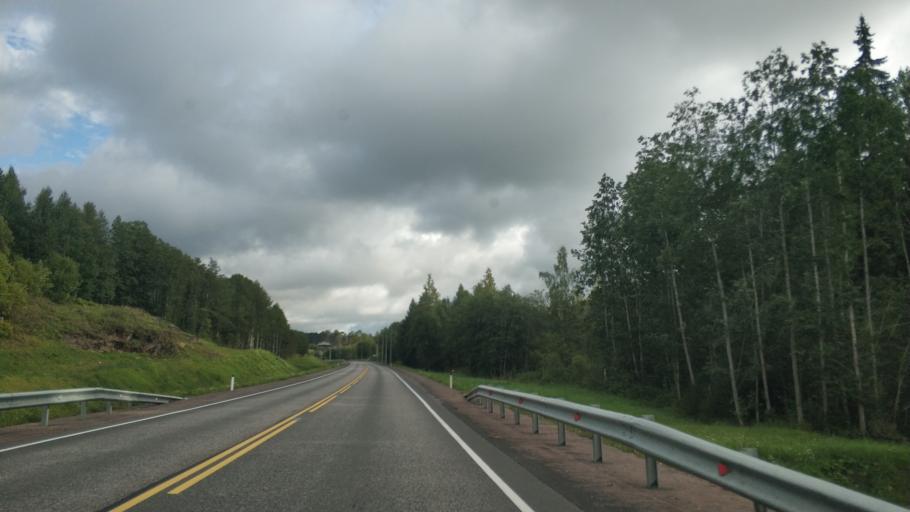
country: RU
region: Republic of Karelia
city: Khelyulya
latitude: 61.8137
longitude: 30.6285
